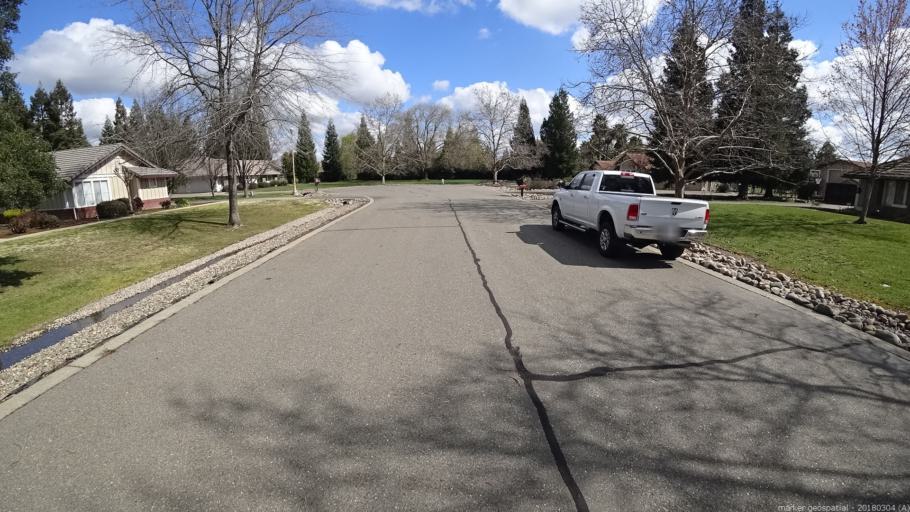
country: US
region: California
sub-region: Sacramento County
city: Vineyard
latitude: 38.4592
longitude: -121.3094
